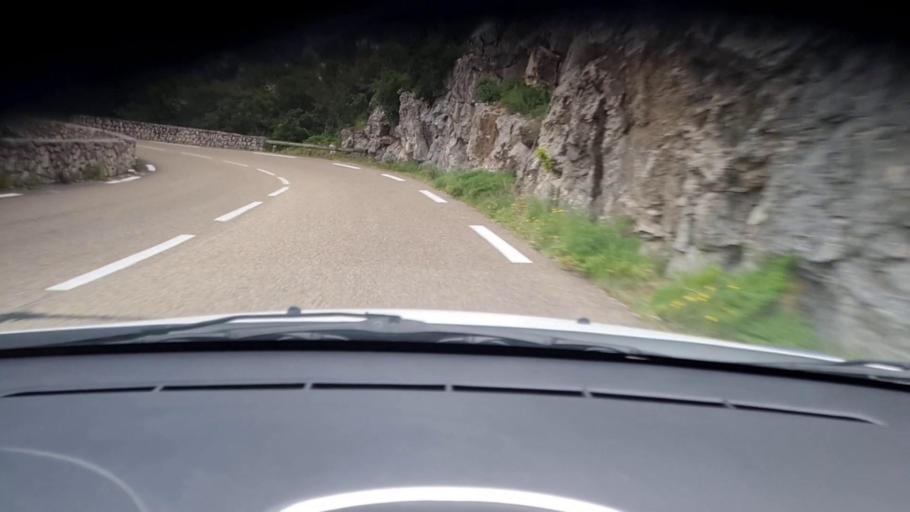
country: FR
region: Languedoc-Roussillon
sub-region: Departement du Gard
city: Blauzac
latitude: 43.9326
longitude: 4.3851
